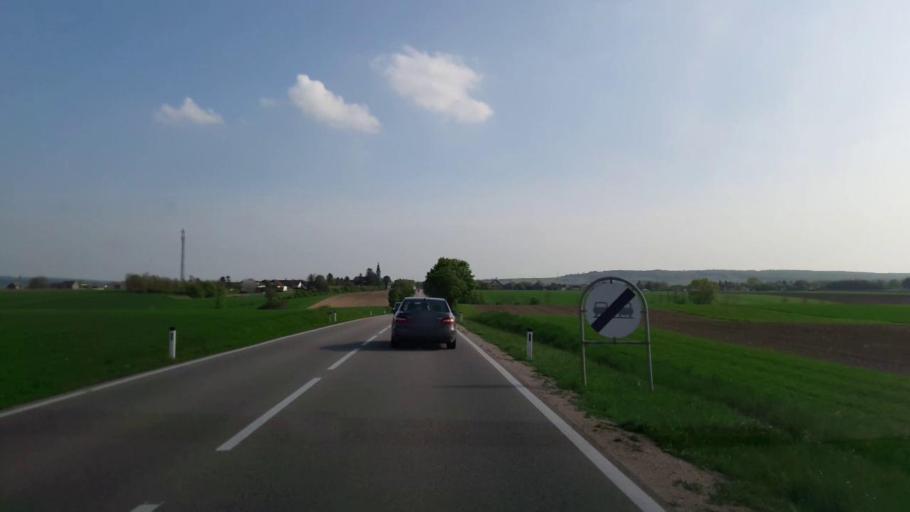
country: AT
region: Lower Austria
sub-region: Politischer Bezirk Hollabrunn
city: Wullersdorf
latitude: 48.6103
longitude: 16.0659
